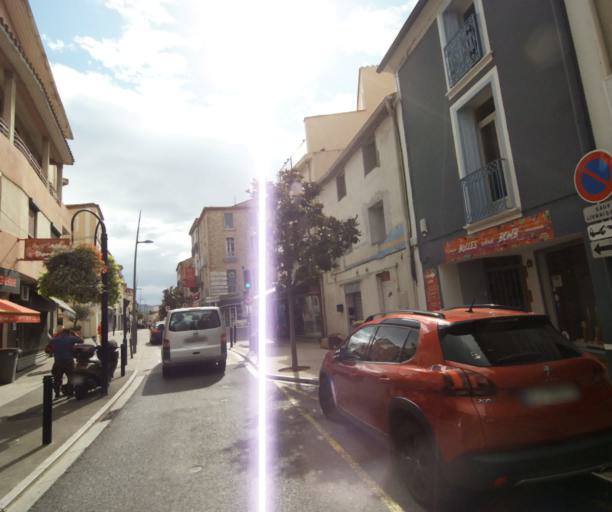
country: FR
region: Languedoc-Roussillon
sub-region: Departement des Pyrenees-Orientales
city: Argelers
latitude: 42.5460
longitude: 3.0220
